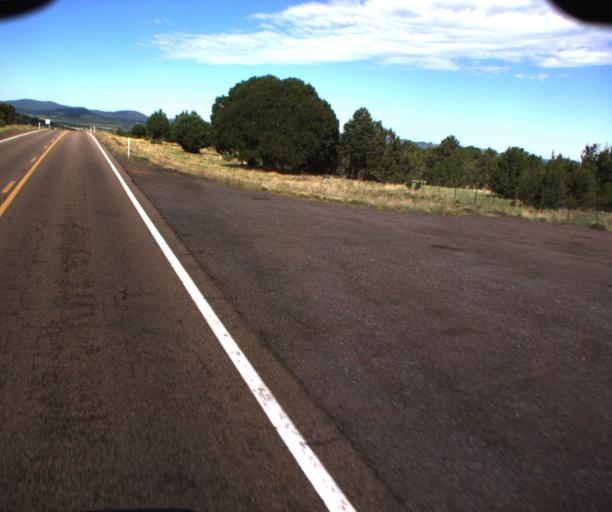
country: US
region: Arizona
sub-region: Apache County
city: Saint Johns
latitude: 34.2678
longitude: -109.6007
